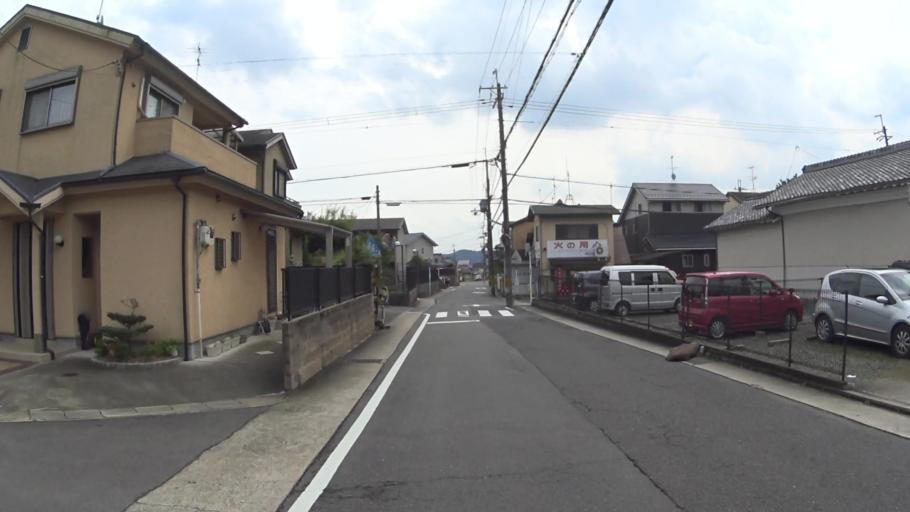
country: JP
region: Kyoto
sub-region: Kyoto-shi
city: Kamigyo-ku
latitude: 35.0777
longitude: 135.7857
